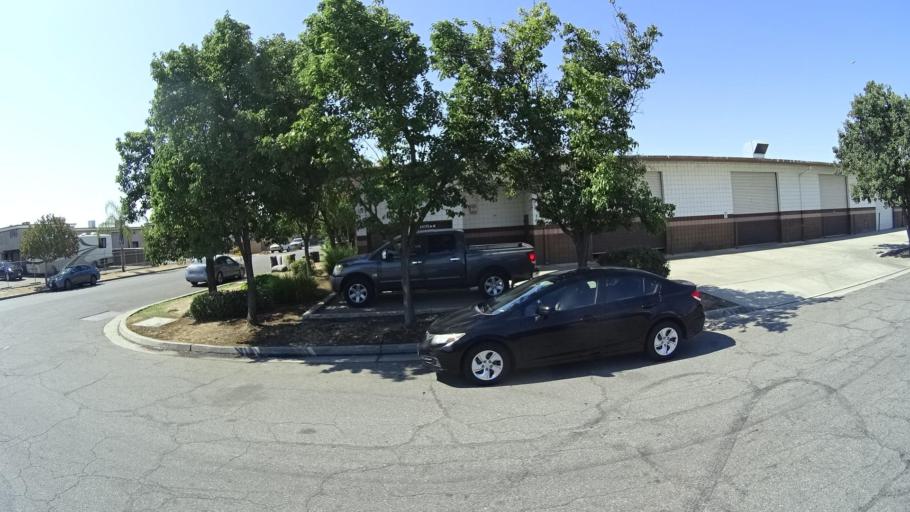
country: US
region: California
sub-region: Fresno County
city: Tarpey Village
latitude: 36.7880
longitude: -119.7300
